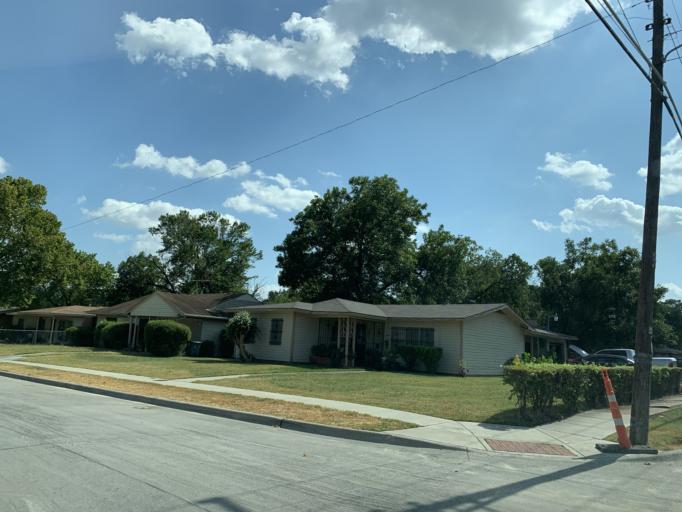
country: US
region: Texas
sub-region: Dallas County
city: Hutchins
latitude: 32.7035
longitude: -96.7735
